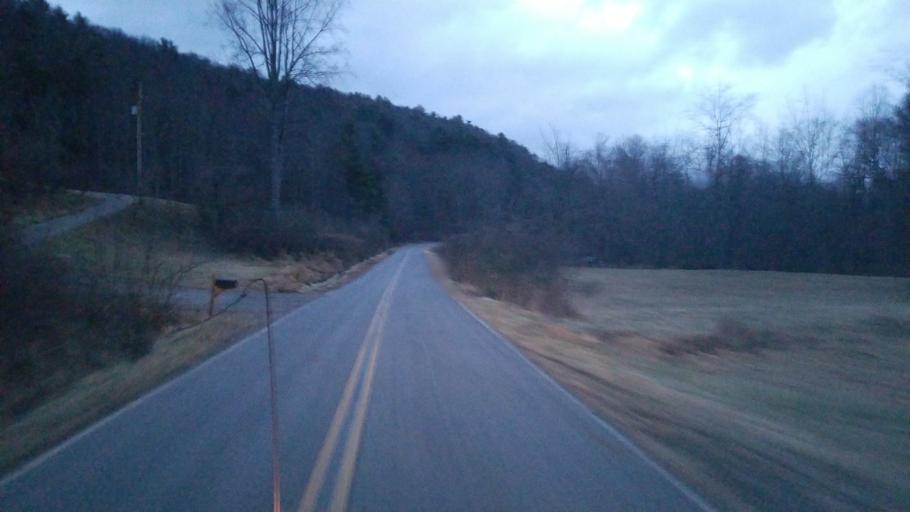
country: US
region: Virginia
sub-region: Pulaski County
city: Pulaski
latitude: 37.1455
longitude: -80.8335
